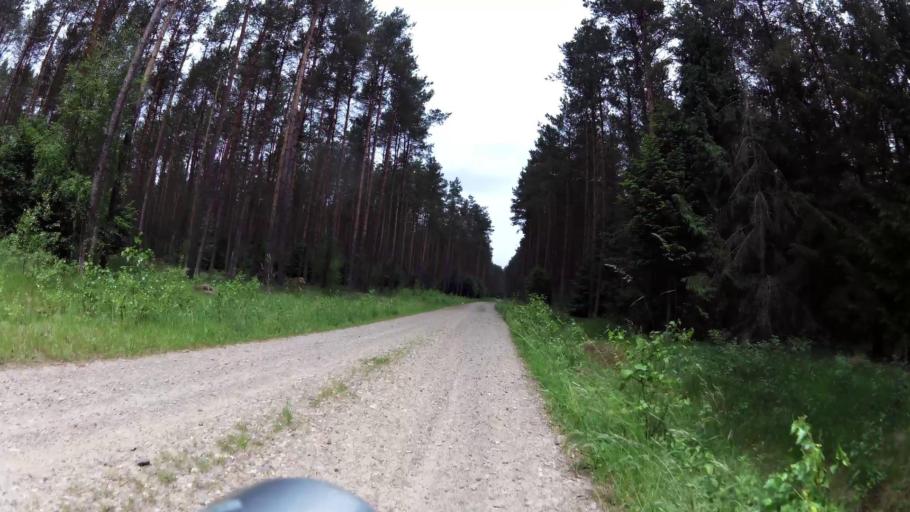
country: PL
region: West Pomeranian Voivodeship
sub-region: Powiat szczecinecki
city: Bialy Bor
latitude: 53.9229
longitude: 16.8353
